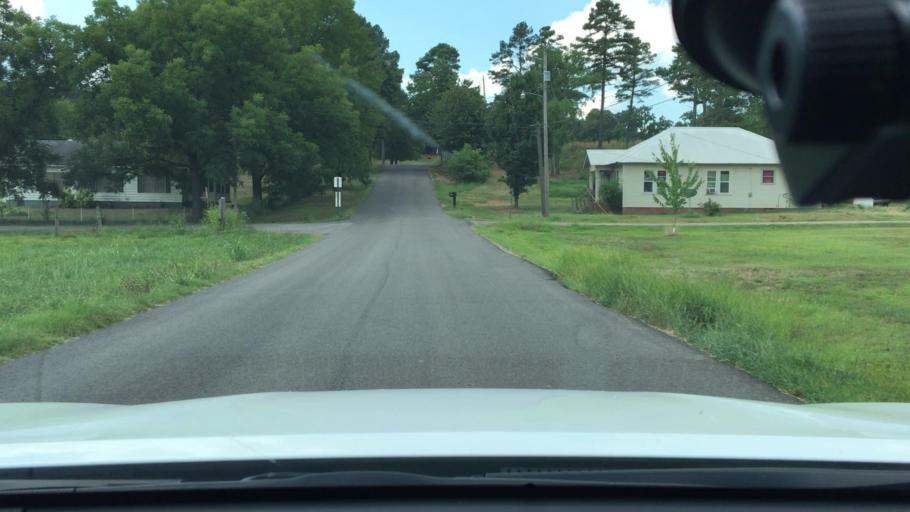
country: US
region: Arkansas
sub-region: Logan County
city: Paris
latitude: 35.2919
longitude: -93.6347
